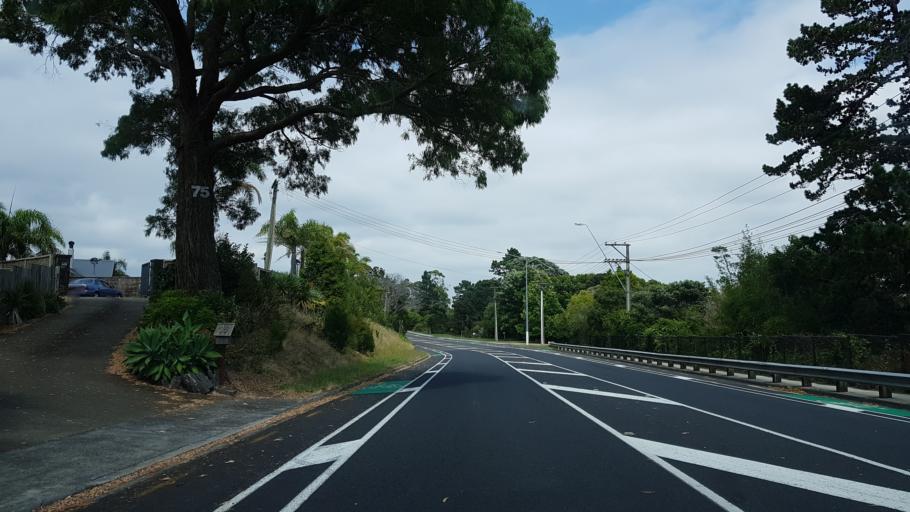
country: NZ
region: Auckland
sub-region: Auckland
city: North Shore
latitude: -36.7786
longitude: 174.6844
